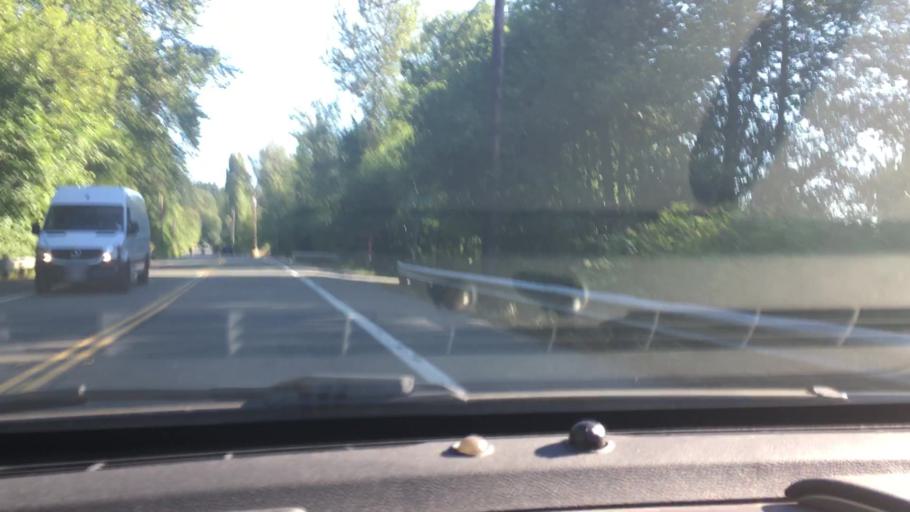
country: US
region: Washington
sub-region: King County
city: West Lake Sammamish
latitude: 47.6010
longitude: -122.0796
